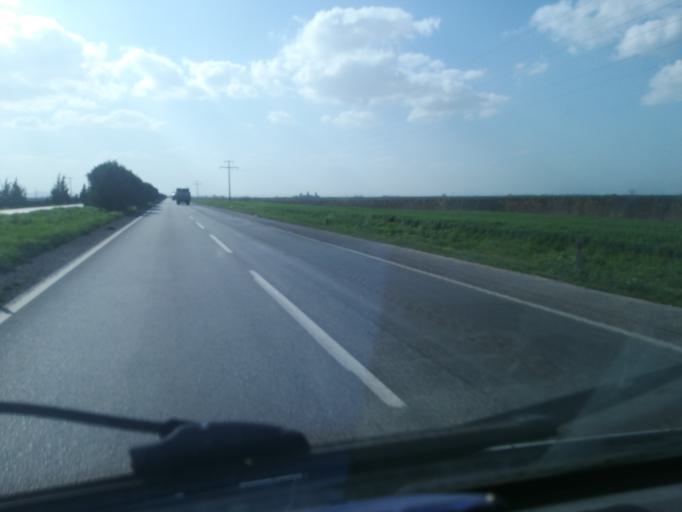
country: TR
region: Adana
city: Ceyhan
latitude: 37.0602
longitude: 35.9149
